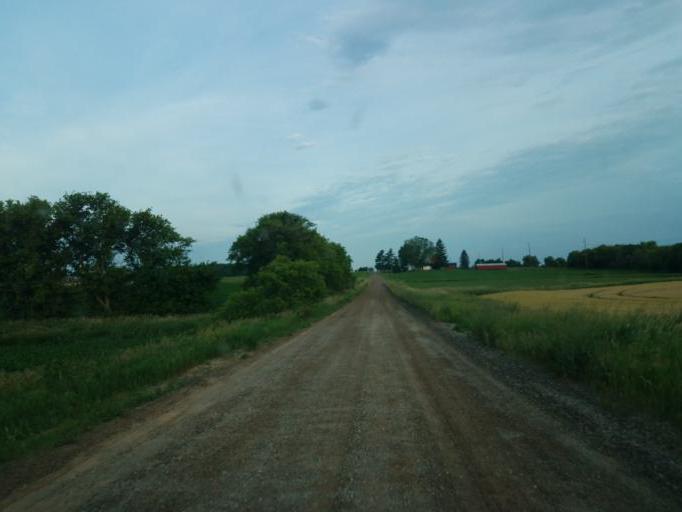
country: US
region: Michigan
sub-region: Eaton County
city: Charlotte
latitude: 42.5973
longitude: -84.9313
